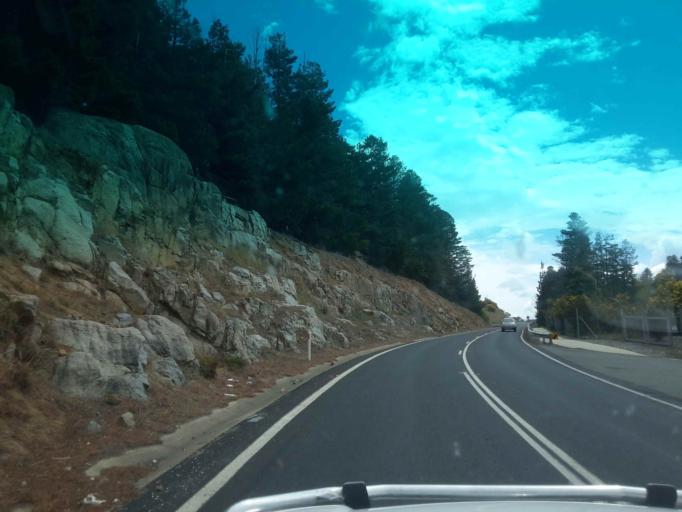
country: AU
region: New South Wales
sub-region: Snowy River
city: Jindabyne
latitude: -36.4345
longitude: 148.6293
